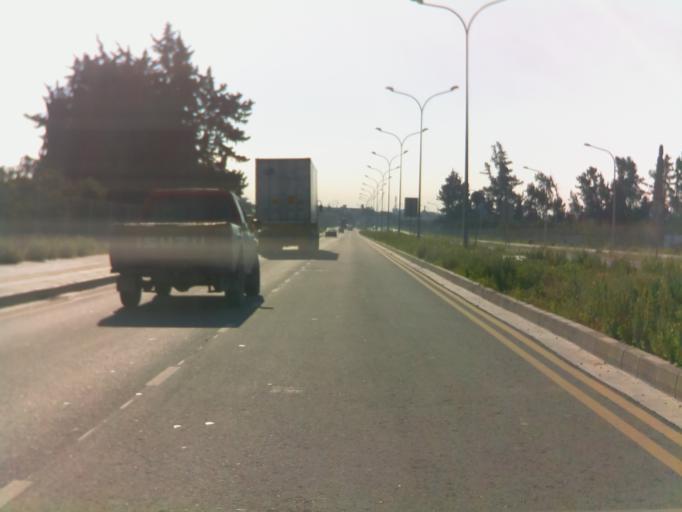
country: CY
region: Limassol
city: Ypsonas
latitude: 34.6636
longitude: 32.9924
